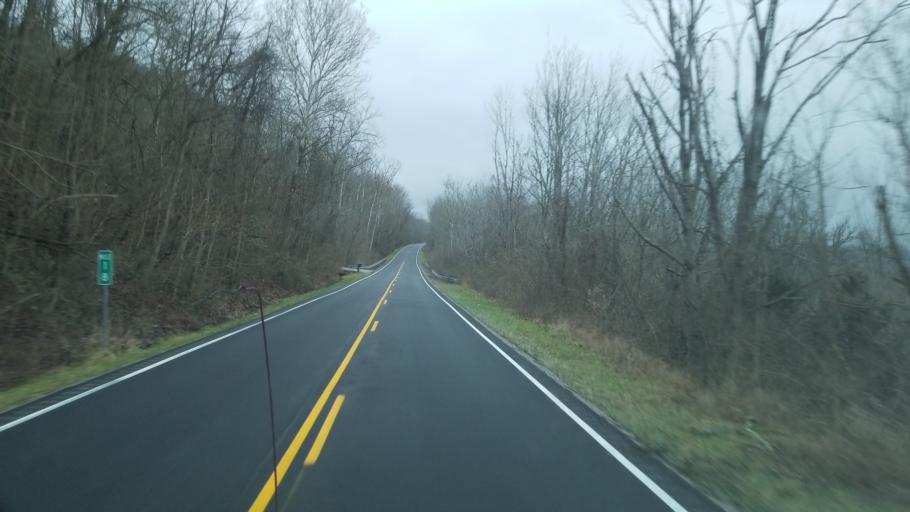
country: US
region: Kentucky
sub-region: Bracken County
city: Augusta
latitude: 38.7664
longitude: -83.9250
